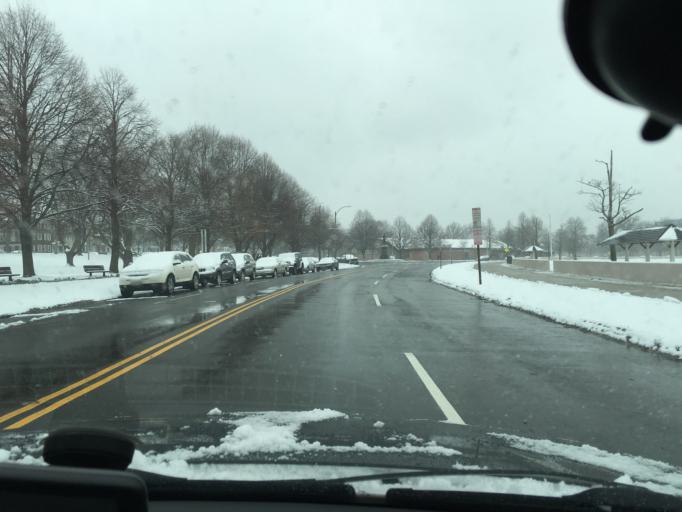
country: US
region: Massachusetts
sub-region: Suffolk County
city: South Boston
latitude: 42.3347
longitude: -71.0237
